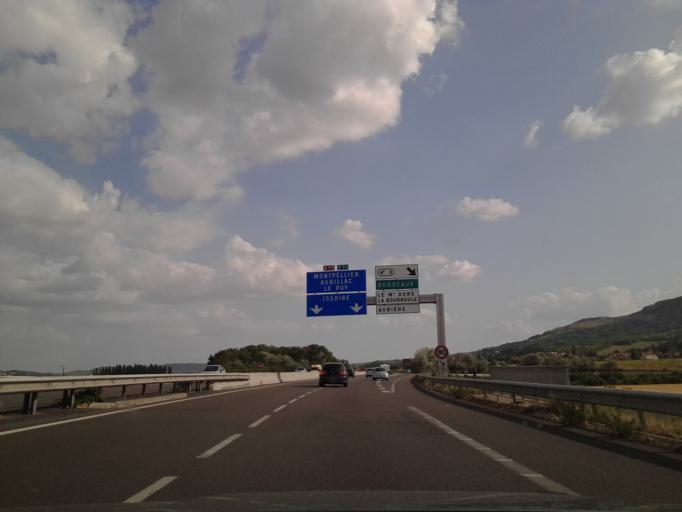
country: FR
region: Auvergne
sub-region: Departement du Puy-de-Dome
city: Perignat-les-Sarlieve
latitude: 45.7465
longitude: 3.1453
